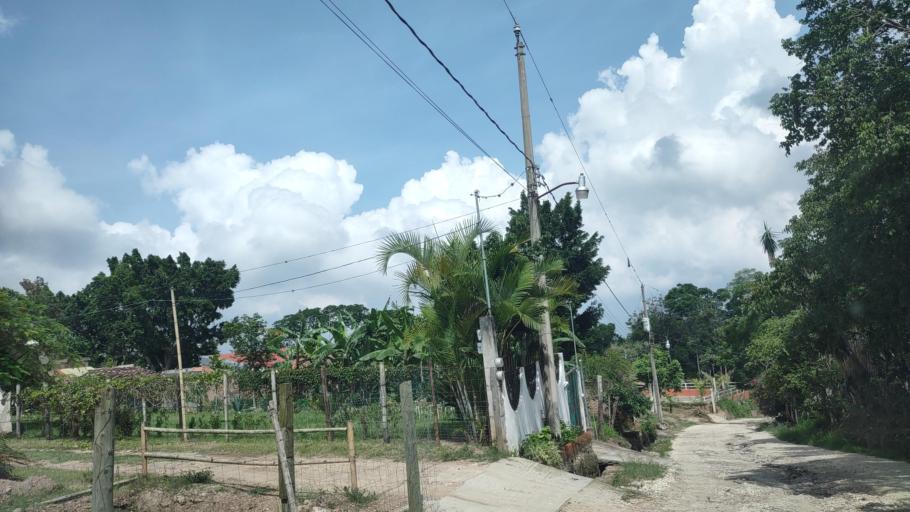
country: MX
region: Veracruz
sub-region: Emiliano Zapata
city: Jacarandas
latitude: 19.4717
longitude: -96.8389
